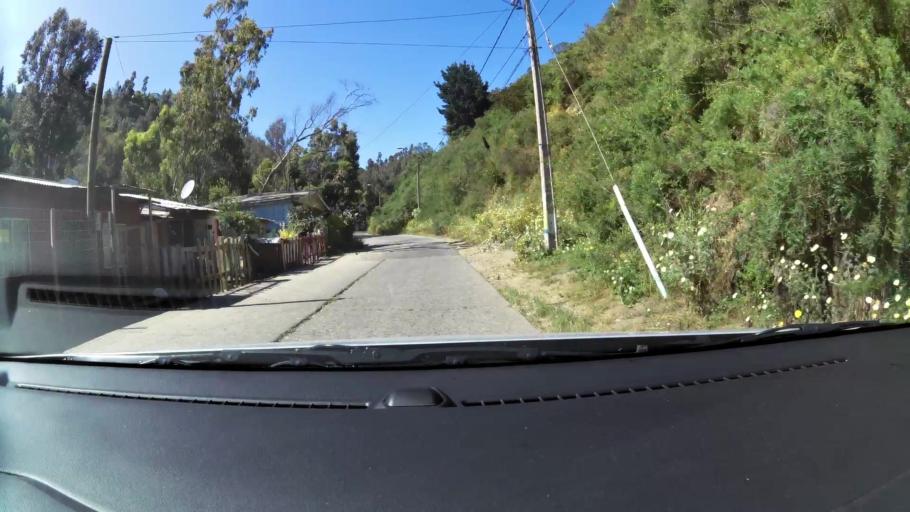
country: CL
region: Valparaiso
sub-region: Provincia de Valparaiso
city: Valparaiso
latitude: -33.0734
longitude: -71.5878
